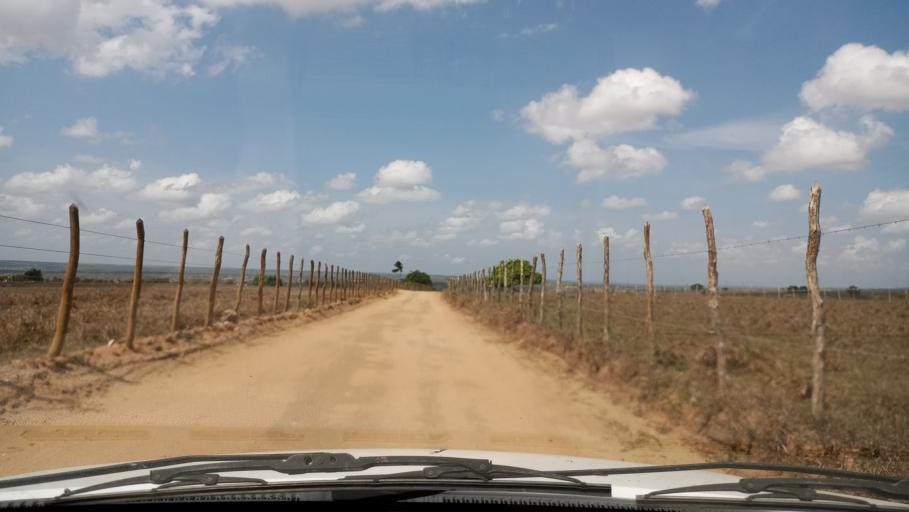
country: BR
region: Rio Grande do Norte
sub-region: Pedro Velho
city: Pedro Velho
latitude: -6.3492
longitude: -35.3317
